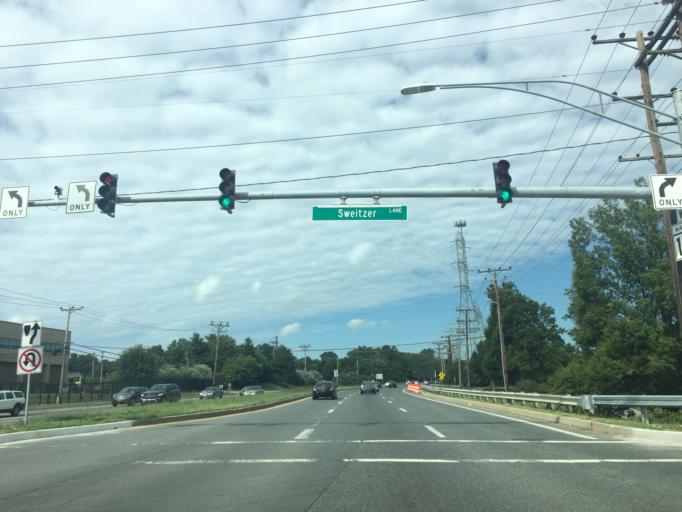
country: US
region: Maryland
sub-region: Prince George's County
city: West Laurel
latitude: 39.0989
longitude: -76.8993
